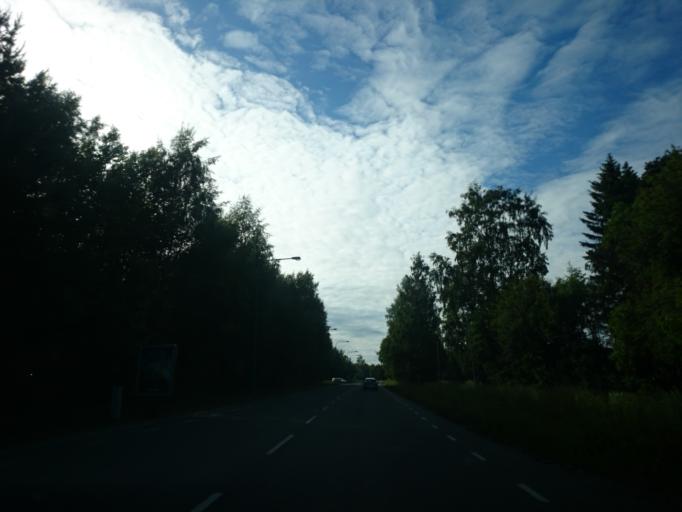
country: SE
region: Vaesternorrland
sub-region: Sundsvalls Kommun
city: Sundsvall
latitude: 62.4020
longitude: 17.3232
